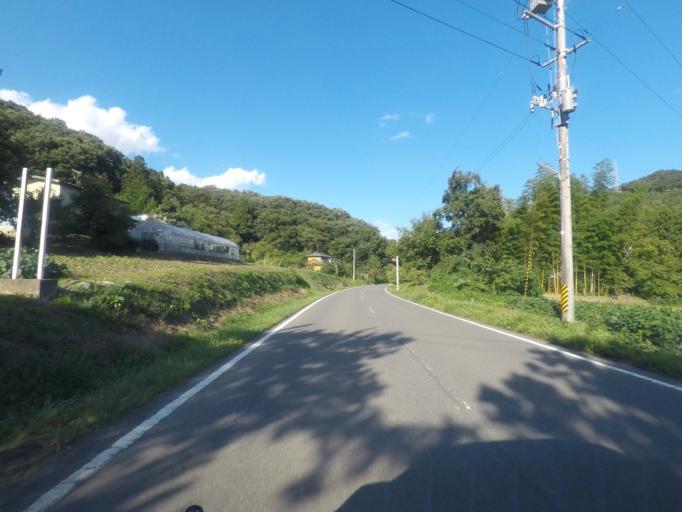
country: JP
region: Fukushima
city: Fukushima-shi
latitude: 37.7211
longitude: 140.5152
